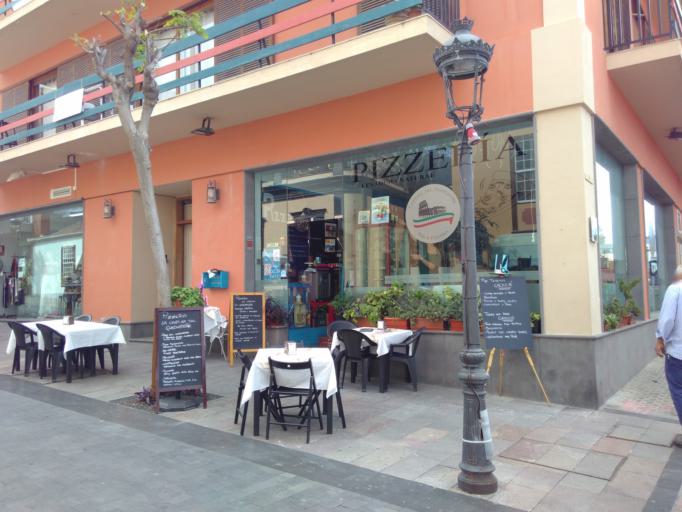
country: ES
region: Canary Islands
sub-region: Provincia de Santa Cruz de Tenerife
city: Los Llanos de Aridane
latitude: 28.6585
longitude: -17.9108
